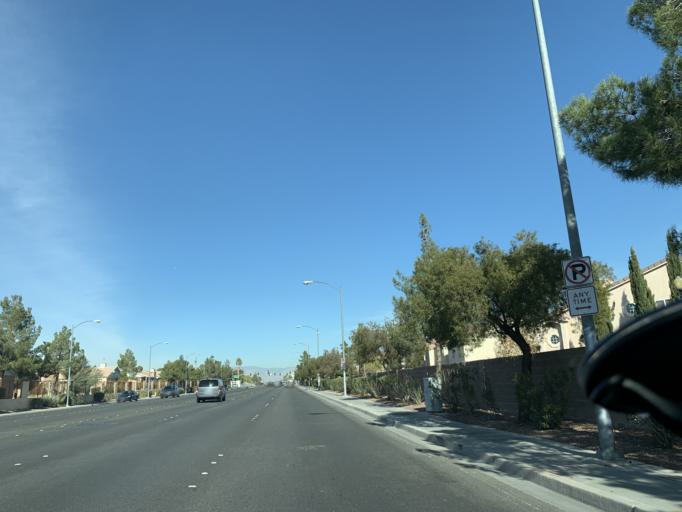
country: US
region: Nevada
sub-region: Clark County
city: Spring Valley
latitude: 36.0901
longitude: -115.2250
